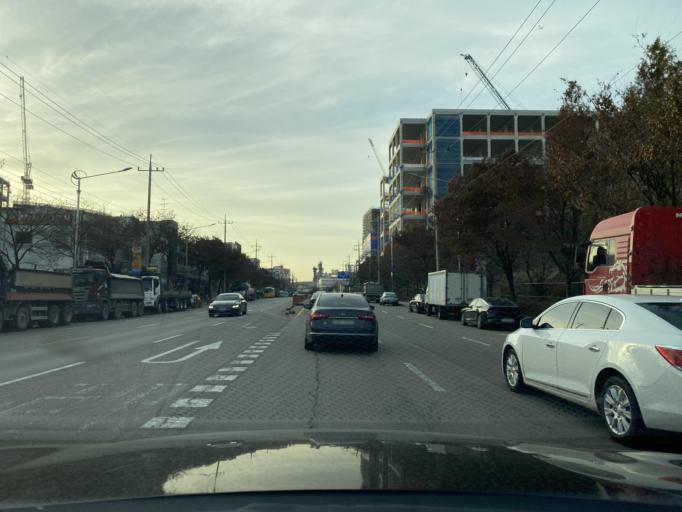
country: KR
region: Incheon
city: Incheon
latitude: 37.5066
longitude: 126.6668
